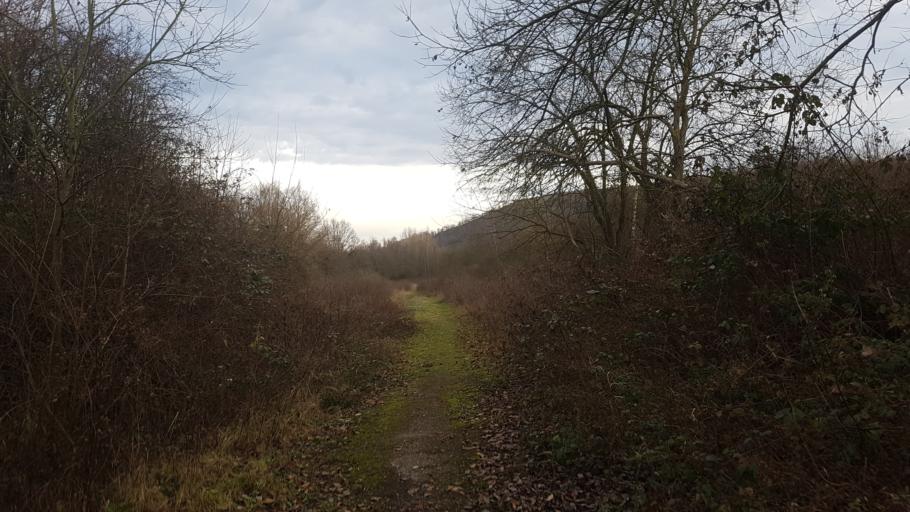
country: DE
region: North Rhine-Westphalia
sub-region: Regierungsbezirk Koln
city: Herzogenrath
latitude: 50.8814
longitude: 6.1268
